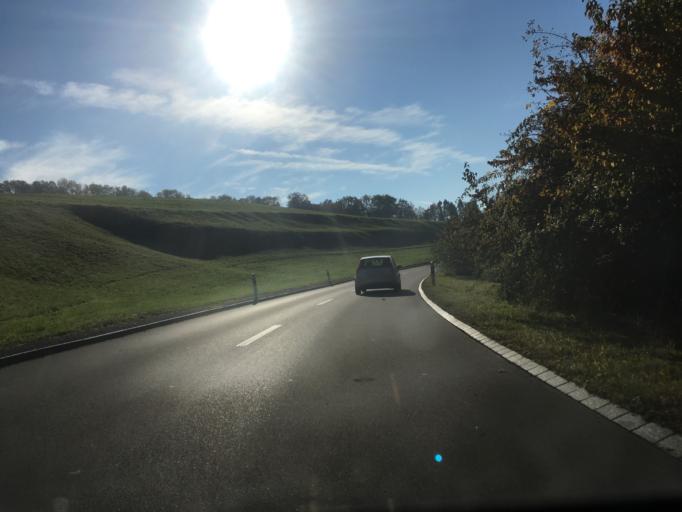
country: CH
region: Zurich
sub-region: Bezirk Dietikon
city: Uitikon
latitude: 47.3573
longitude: 8.4661
